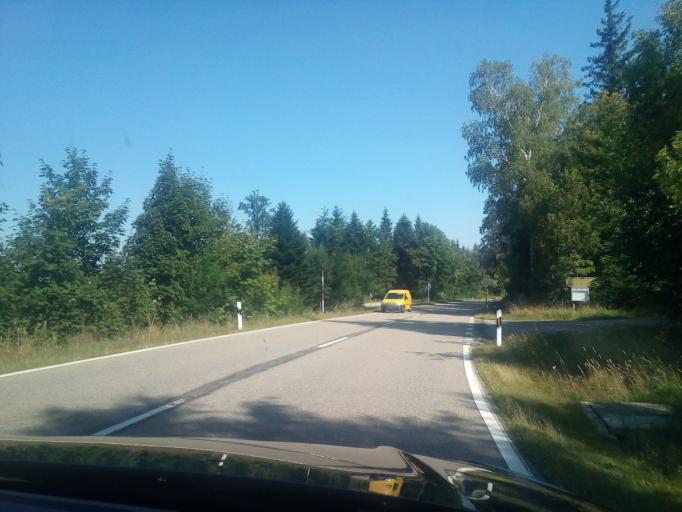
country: DE
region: Baden-Wuerttemberg
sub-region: Karlsruhe Region
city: Buhlertal
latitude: 48.6673
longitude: 8.2319
